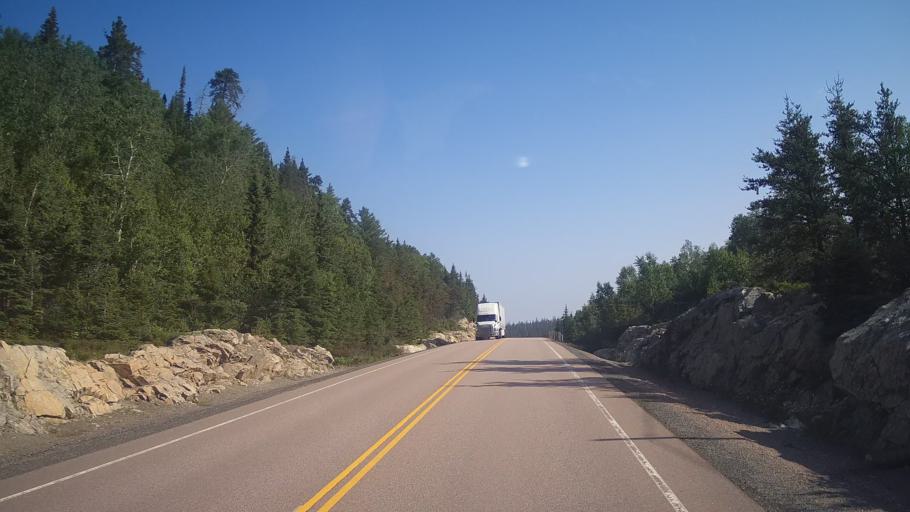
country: CA
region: Ontario
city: Rayside-Balfour
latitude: 46.9910
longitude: -81.6329
